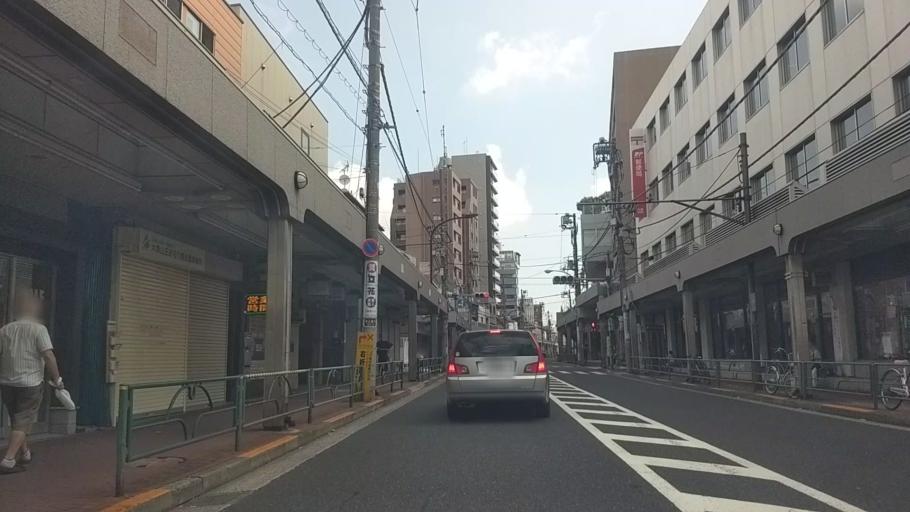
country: JP
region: Kanagawa
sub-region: Kawasaki-shi
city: Kawasaki
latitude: 35.5825
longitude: 139.7226
